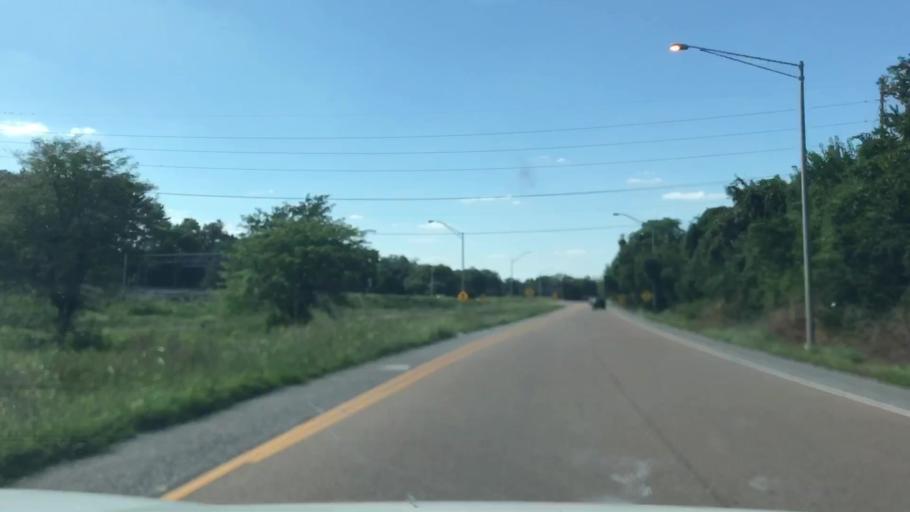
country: US
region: Illinois
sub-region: Saint Clair County
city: Alorton
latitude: 38.5486
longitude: -90.0663
